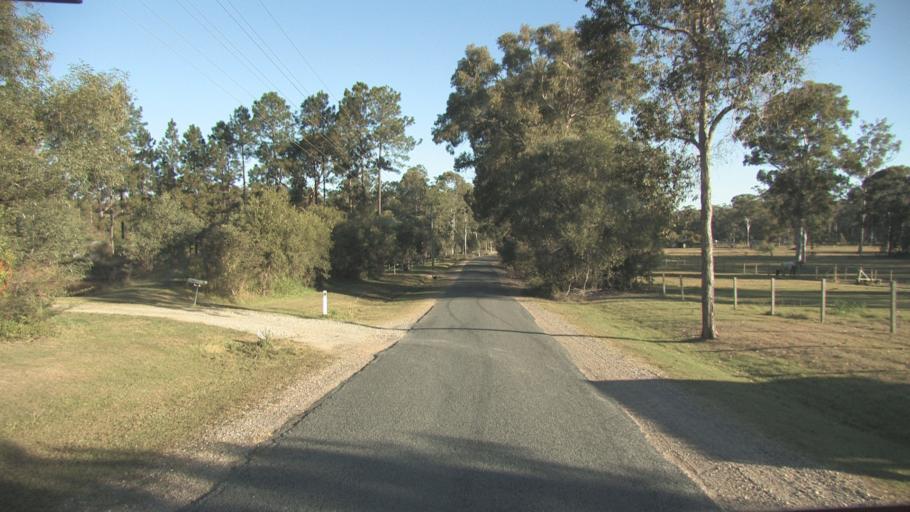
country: AU
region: Queensland
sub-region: Logan
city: Chambers Flat
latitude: -27.7749
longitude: 153.1289
